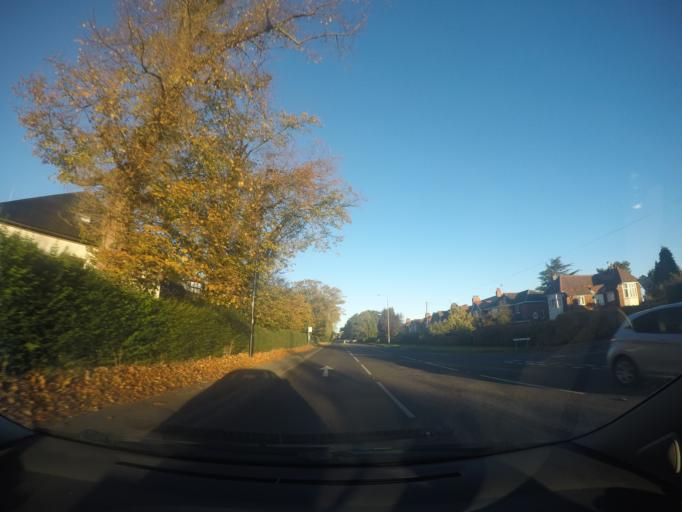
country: GB
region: England
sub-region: City of York
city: Skelton
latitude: 53.9776
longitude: -1.1098
